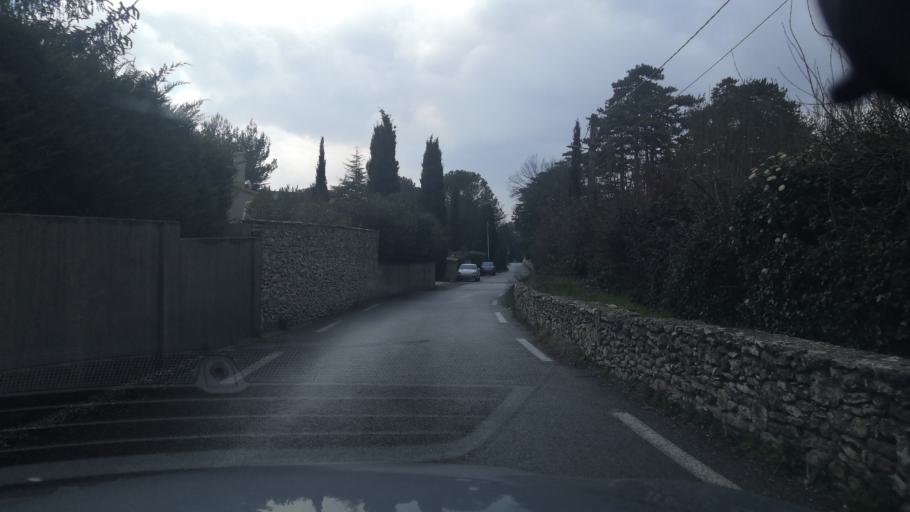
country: FR
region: Provence-Alpes-Cote d'Azur
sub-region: Departement des Bouches-du-Rhone
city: Aix-en-Provence
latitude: 43.5605
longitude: 5.4158
